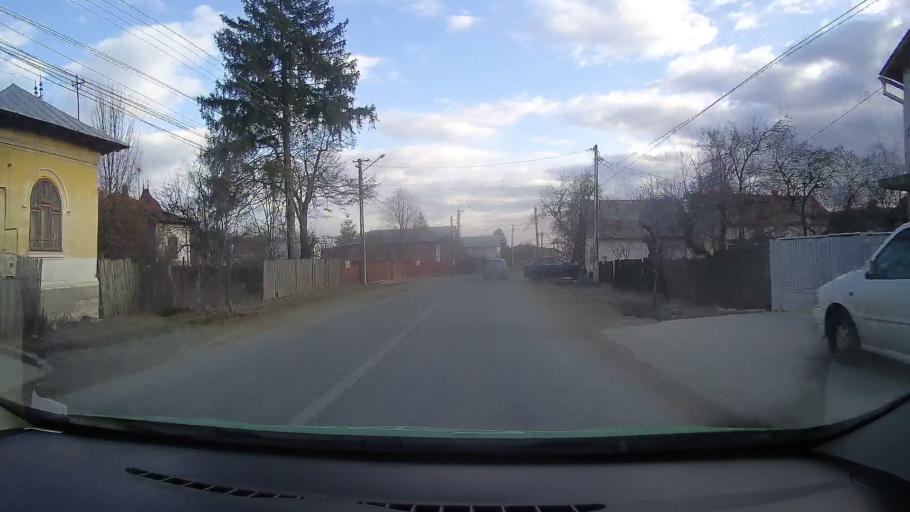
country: RO
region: Dambovita
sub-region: Comuna Gura Ocnitei
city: Gura Ocnitei
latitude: 44.9485
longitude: 25.5589
